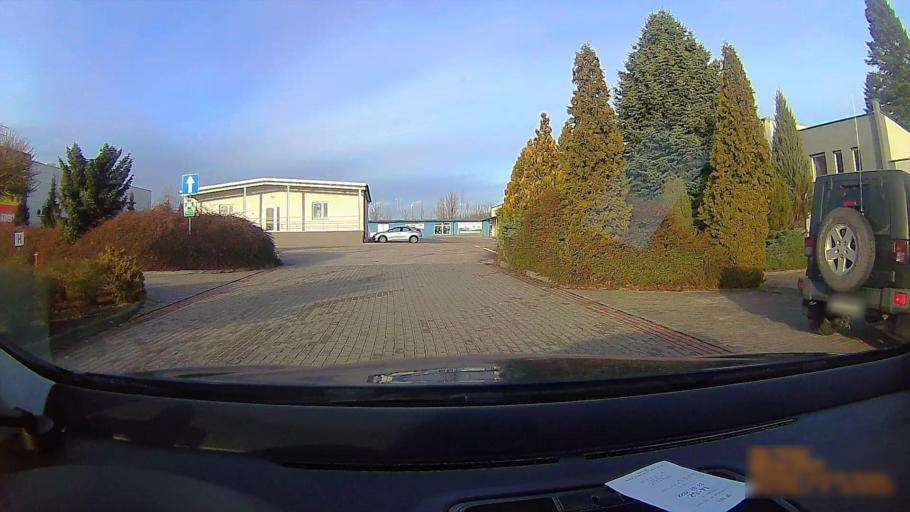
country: PL
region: Greater Poland Voivodeship
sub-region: Konin
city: Konin
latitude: 52.2316
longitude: 18.2370
